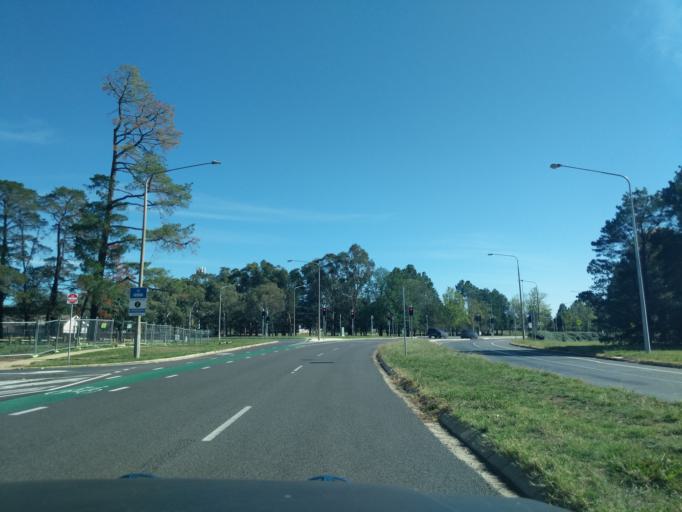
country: AU
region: Australian Capital Territory
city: Forrest
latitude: -35.3357
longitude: 149.1479
